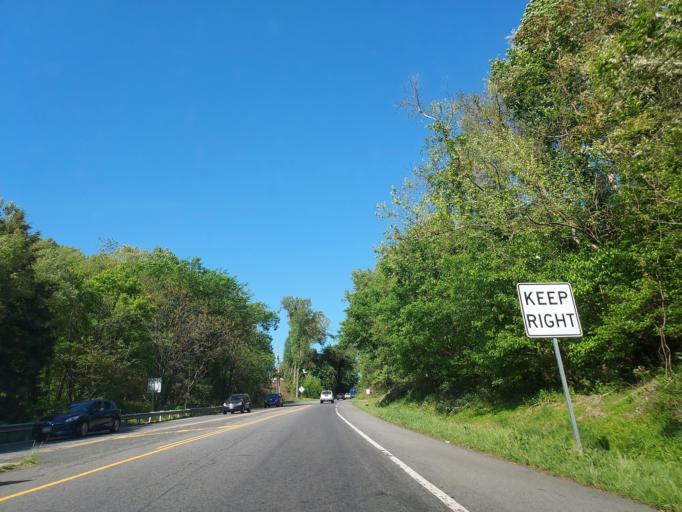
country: US
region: Virginia
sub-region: City of Lynchburg
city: Lynchburg
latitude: 37.4212
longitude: -79.1352
